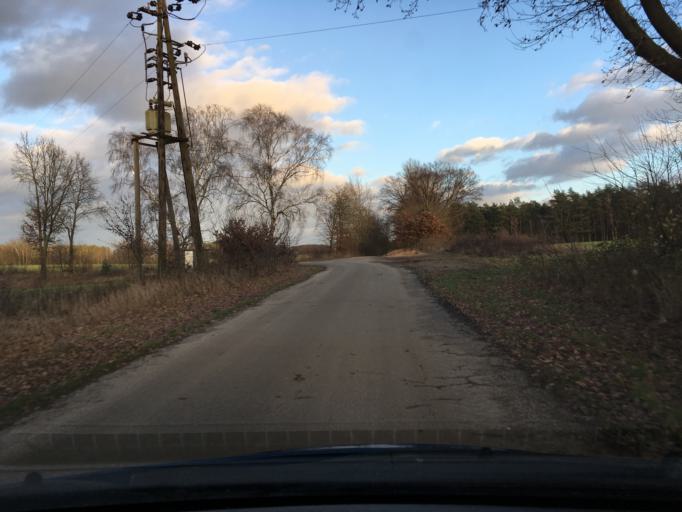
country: DE
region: Lower Saxony
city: Soderstorf
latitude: 53.1156
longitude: 10.1670
